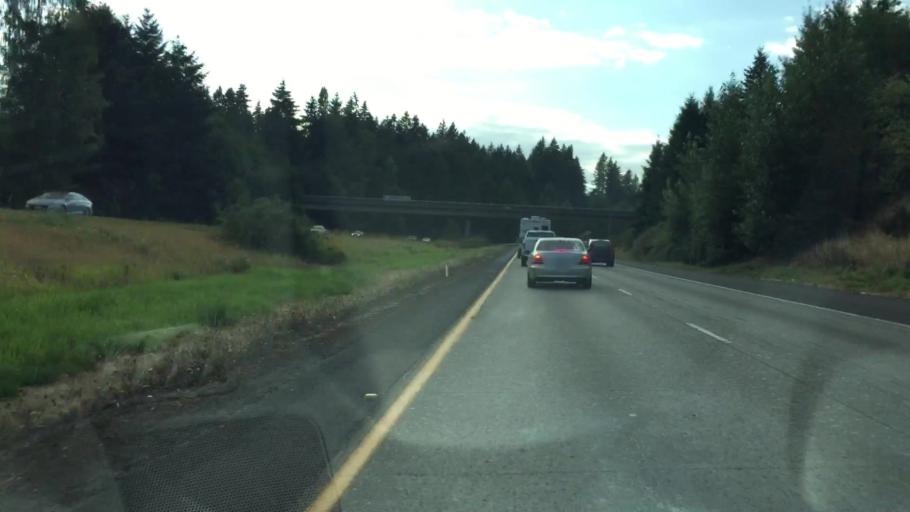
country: US
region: Washington
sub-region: Clark County
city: Barberton
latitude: 45.6992
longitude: -122.6183
